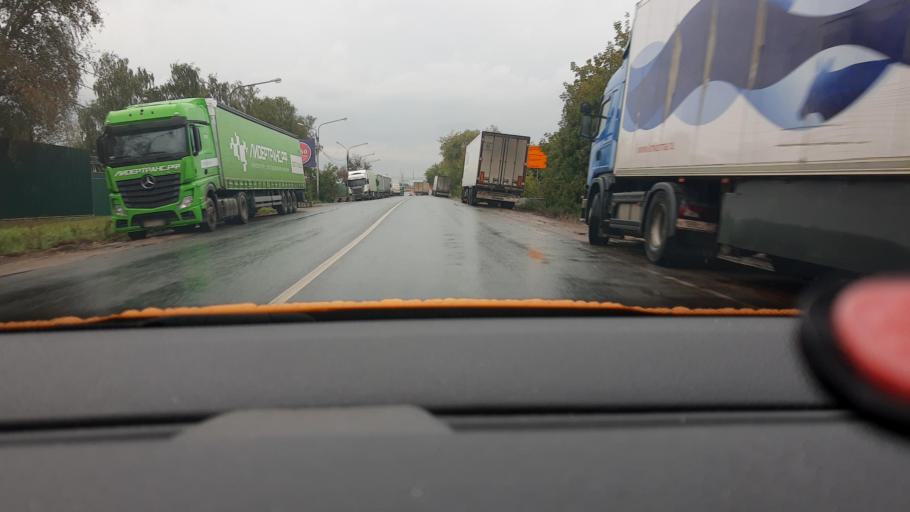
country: RU
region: Moskovskaya
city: Obukhovo
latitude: 55.8236
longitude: 38.2620
